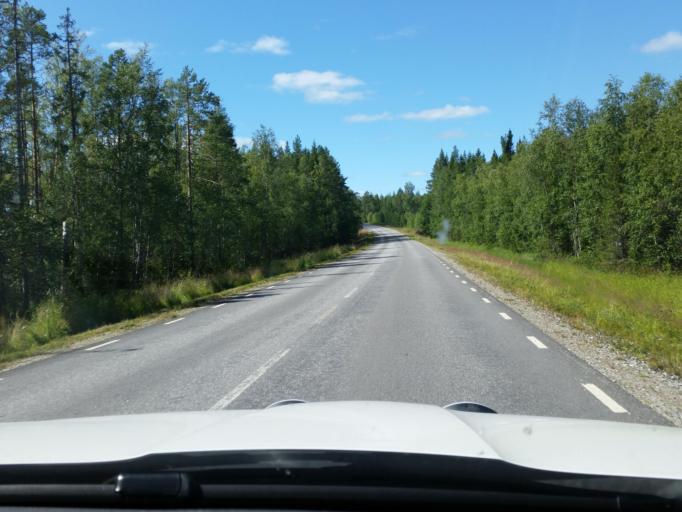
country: SE
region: Norrbotten
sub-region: Pitea Kommun
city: Hortlax
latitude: 65.2193
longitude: 21.2620
